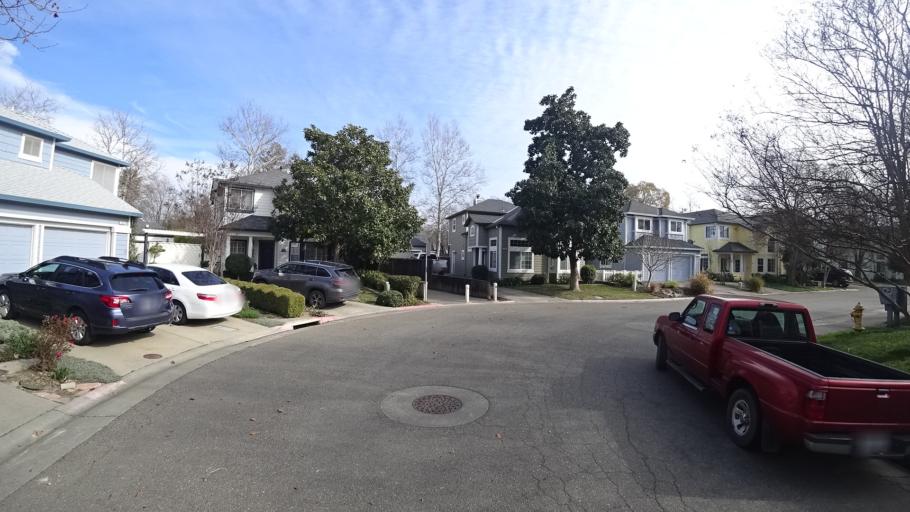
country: US
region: California
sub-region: Yolo County
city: Davis
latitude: 38.5429
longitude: -121.7215
